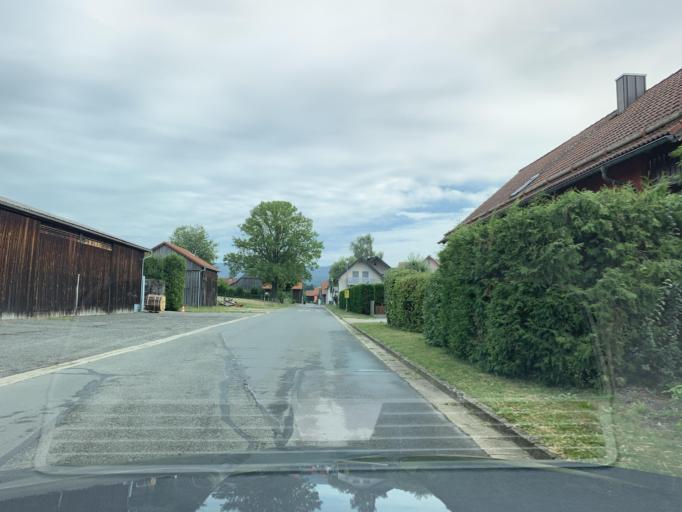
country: DE
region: Bavaria
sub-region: Upper Palatinate
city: Winklarn
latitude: 49.4145
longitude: 12.5110
